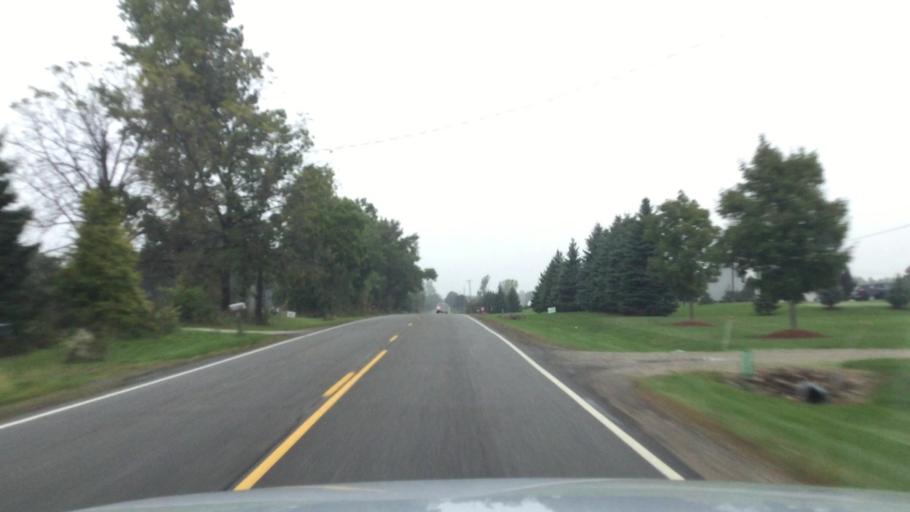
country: US
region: Michigan
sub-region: Shiawassee County
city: Corunna
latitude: 42.9136
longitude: -84.1239
